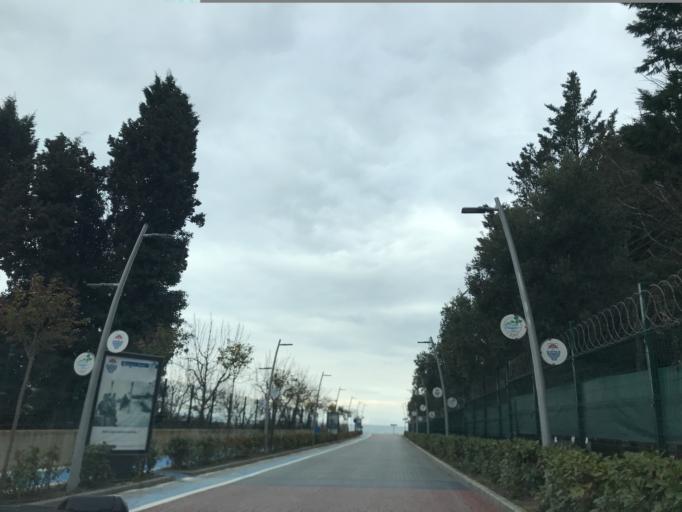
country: TR
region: Yalova
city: Ciftlikkoy
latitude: 40.6640
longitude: 29.3007
